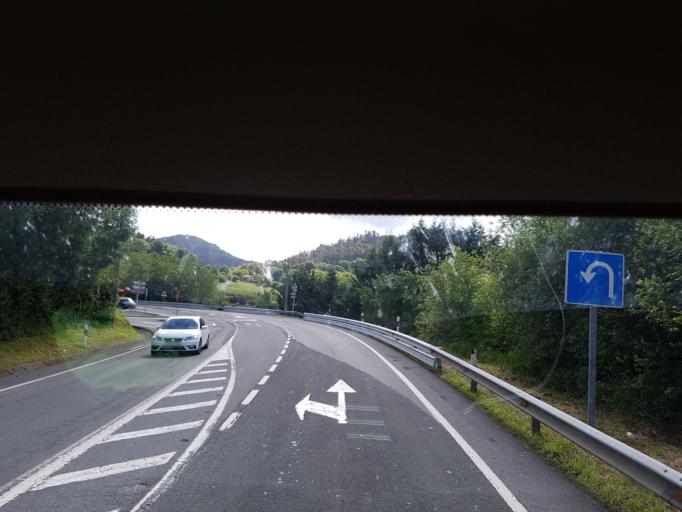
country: ES
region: Basque Country
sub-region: Bizkaia
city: Sopuerta
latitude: 43.2716
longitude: -3.1524
